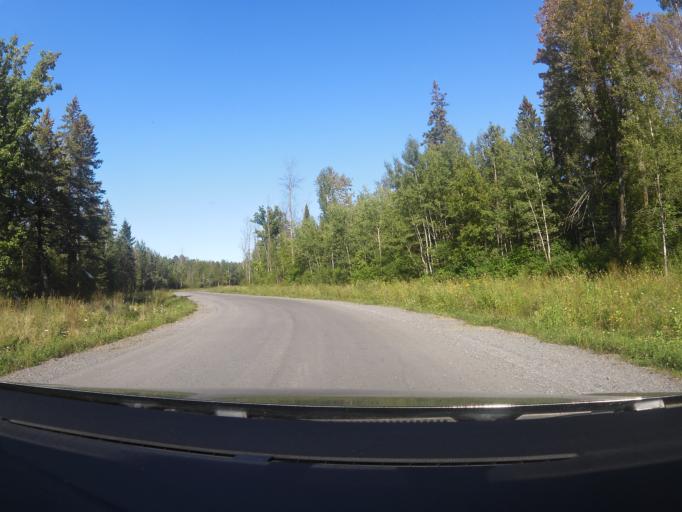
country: CA
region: Ontario
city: Carleton Place
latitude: 45.3100
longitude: -76.0694
